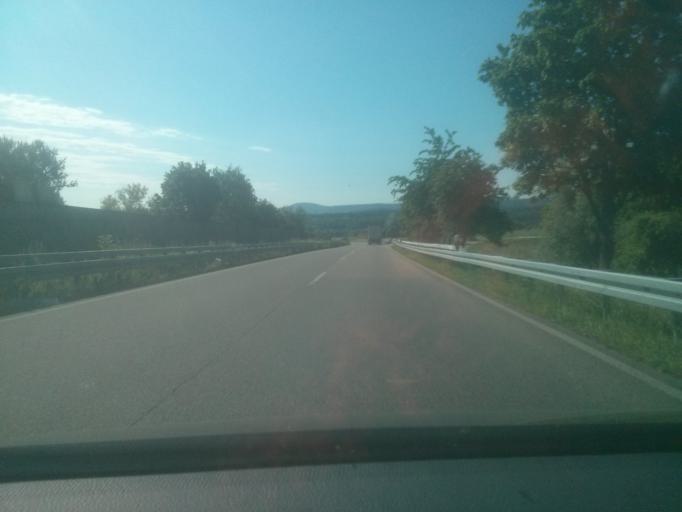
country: DE
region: Baden-Wuerttemberg
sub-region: Tuebingen Region
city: Kusterdingen
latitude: 48.5017
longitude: 9.1227
